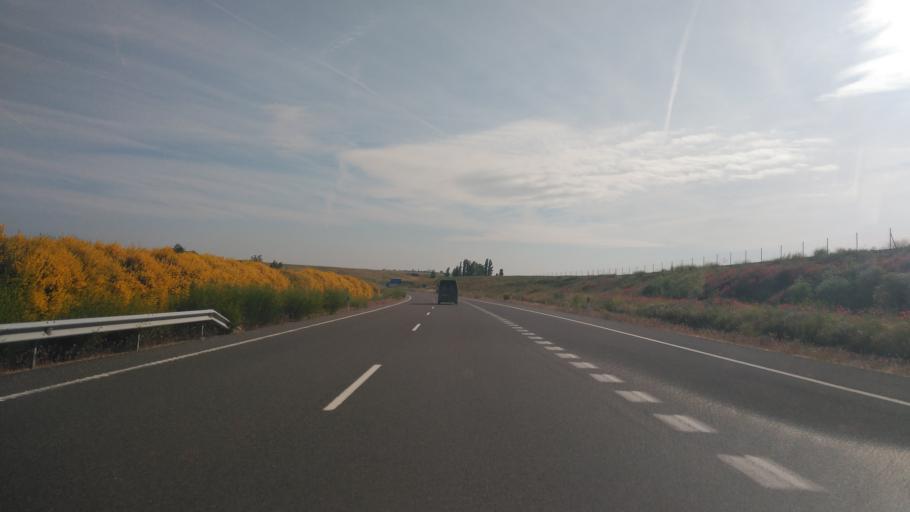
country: ES
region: Castille and Leon
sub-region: Provincia de Salamanca
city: Monterrubio de Armuna
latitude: 41.0334
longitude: -5.6709
